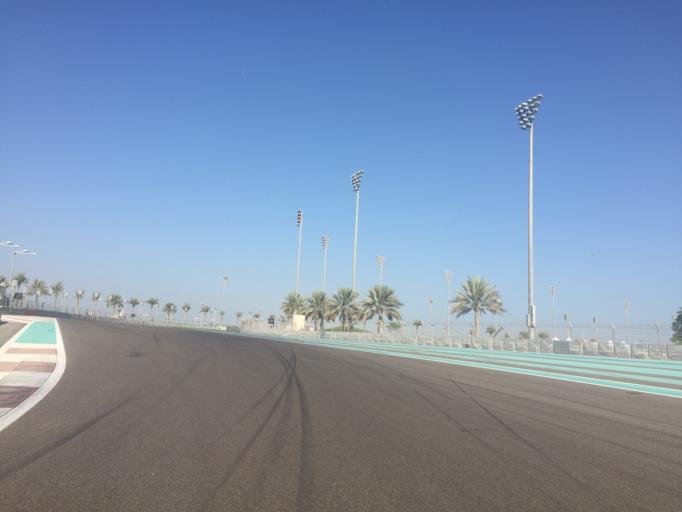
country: AE
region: Abu Dhabi
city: Abu Dhabi
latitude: 24.4726
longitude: 54.6075
